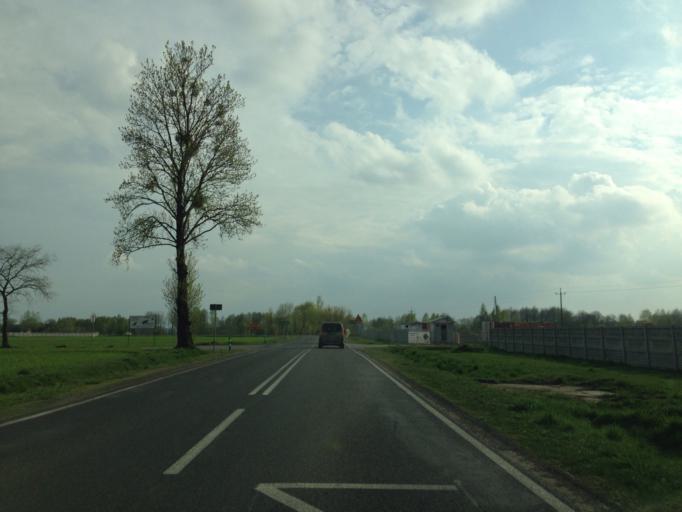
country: PL
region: Masovian Voivodeship
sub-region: Powiat zurominski
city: Zuromin
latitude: 53.0313
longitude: 19.9106
